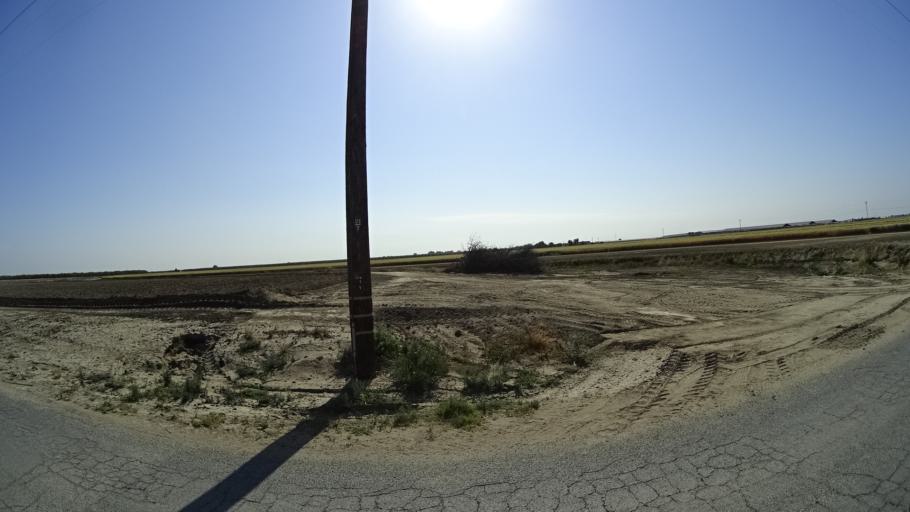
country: US
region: California
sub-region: Kings County
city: Home Garden
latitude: 36.2571
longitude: -119.5831
